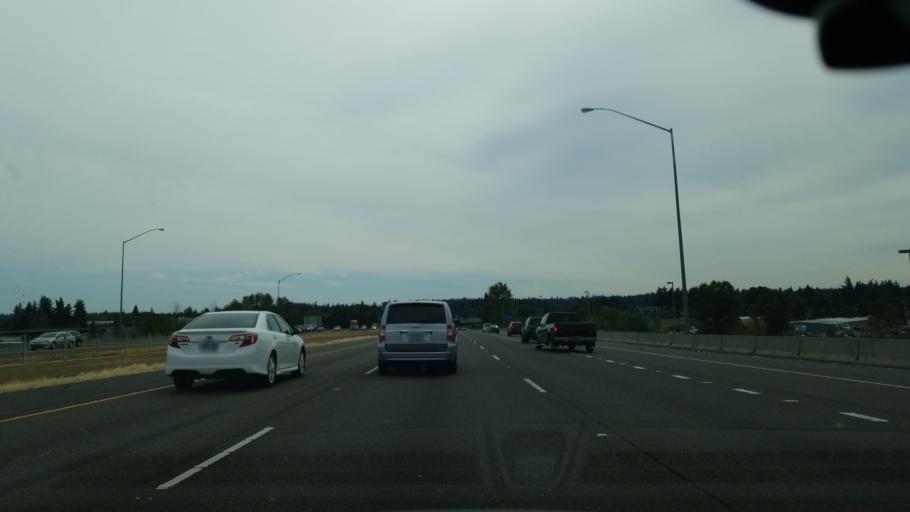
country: US
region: Oregon
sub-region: Clackamas County
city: Clackamas
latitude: 45.4254
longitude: -122.5688
